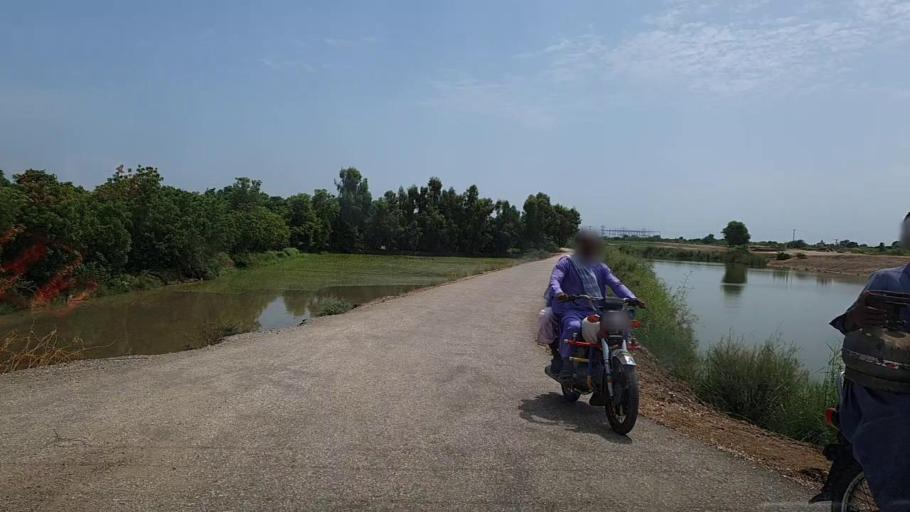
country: PK
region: Sindh
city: Bhiria
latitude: 26.9053
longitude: 68.2015
